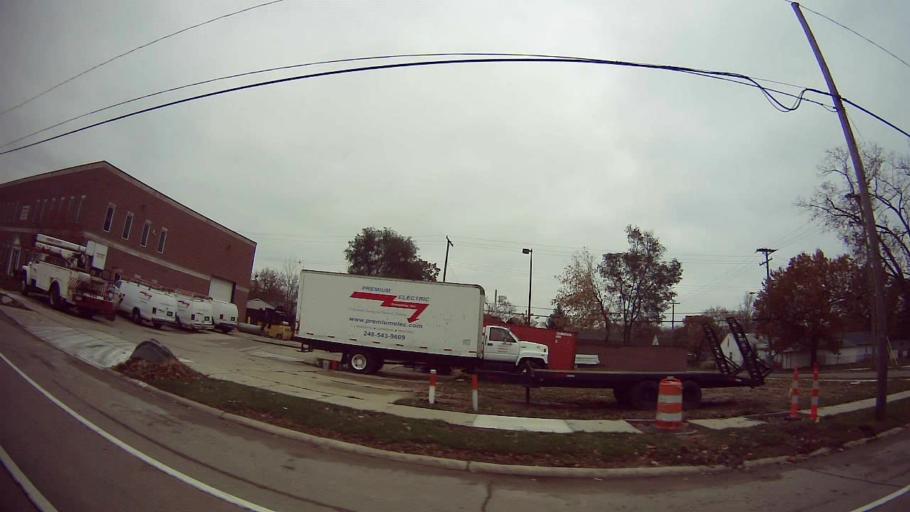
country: US
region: Michigan
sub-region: Oakland County
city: Ferndale
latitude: 42.4650
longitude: -83.1232
